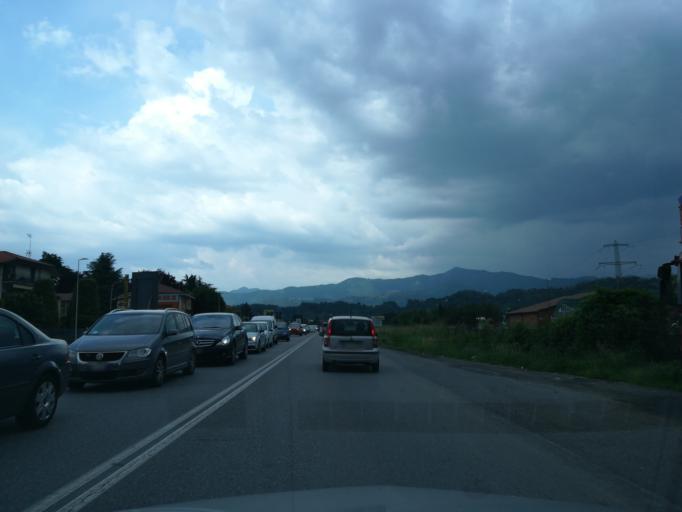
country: IT
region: Lombardy
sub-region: Provincia di Bergamo
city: Scano al Brembo
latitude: 45.7119
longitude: 9.6091
